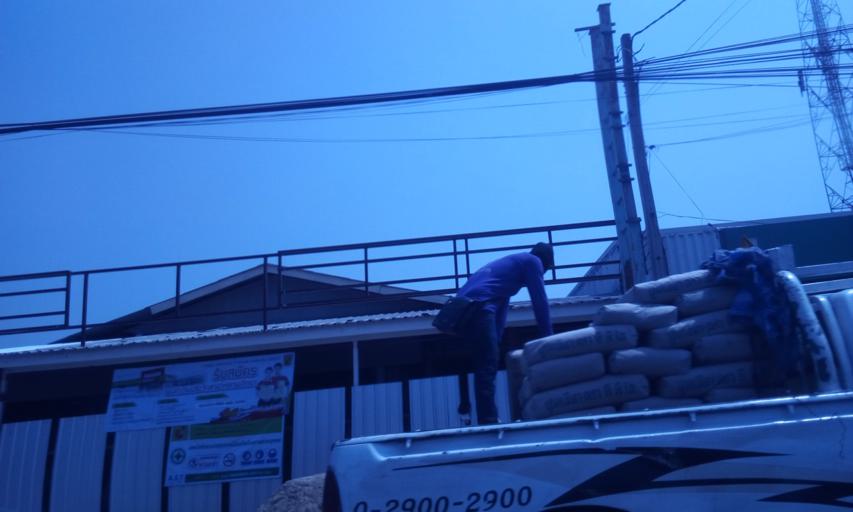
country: TH
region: Nonthaburi
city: Bang Yai
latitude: 13.9092
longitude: 100.3539
